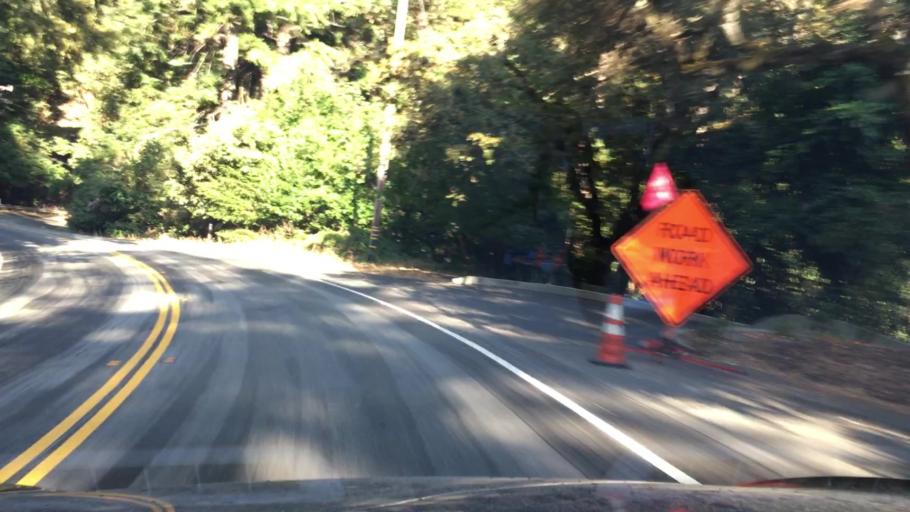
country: US
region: California
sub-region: San Mateo County
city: Woodside
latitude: 37.3921
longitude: -122.2855
